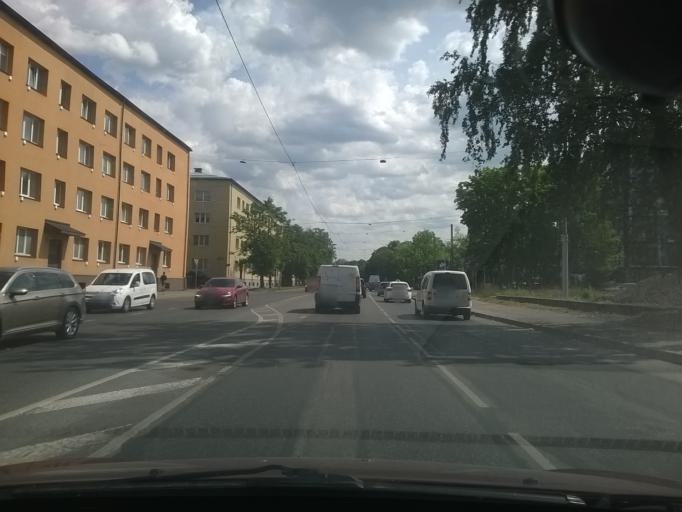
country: EE
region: Harju
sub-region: Tallinna linn
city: Tallinn
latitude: 59.4289
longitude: 24.7070
